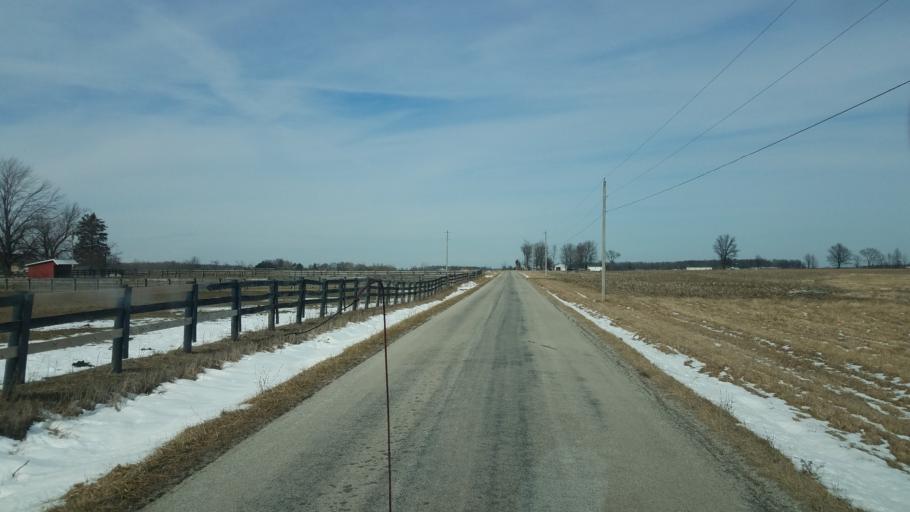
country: US
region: Ohio
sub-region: Delaware County
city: Ashley
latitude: 40.3993
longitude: -82.9358
